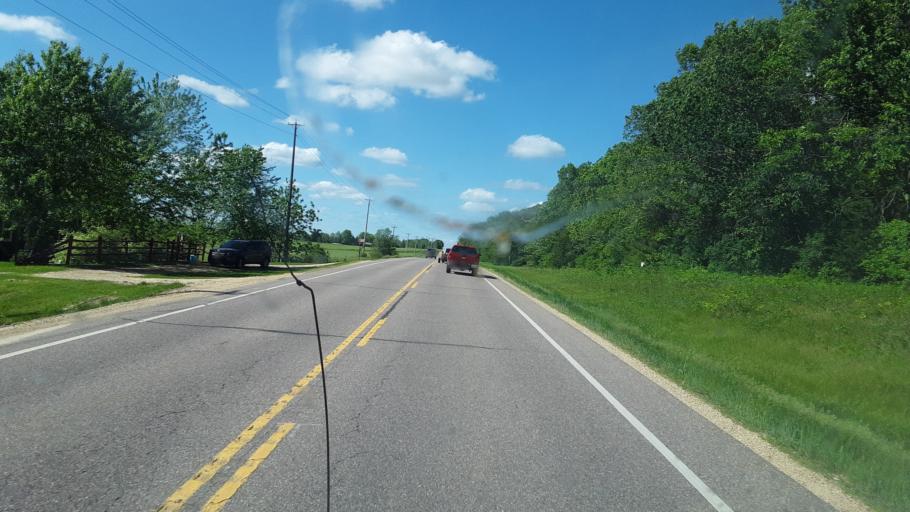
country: US
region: Wisconsin
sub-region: Juneau County
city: Mauston
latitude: 43.7702
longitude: -90.0771
